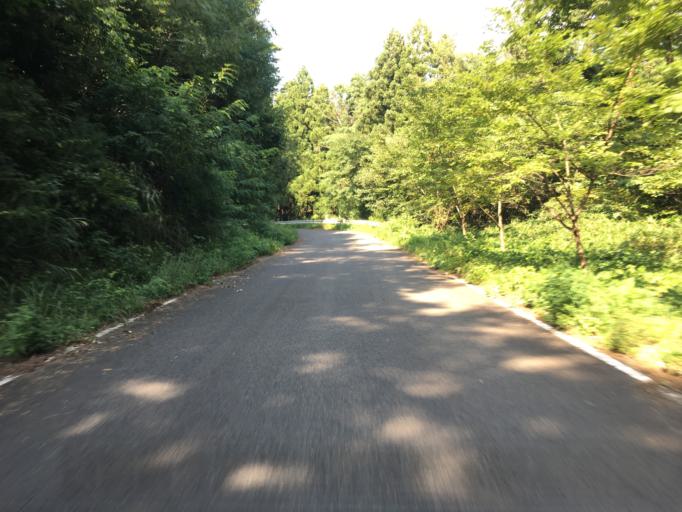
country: JP
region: Fukushima
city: Nihommatsu
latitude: 37.6054
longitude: 140.3851
